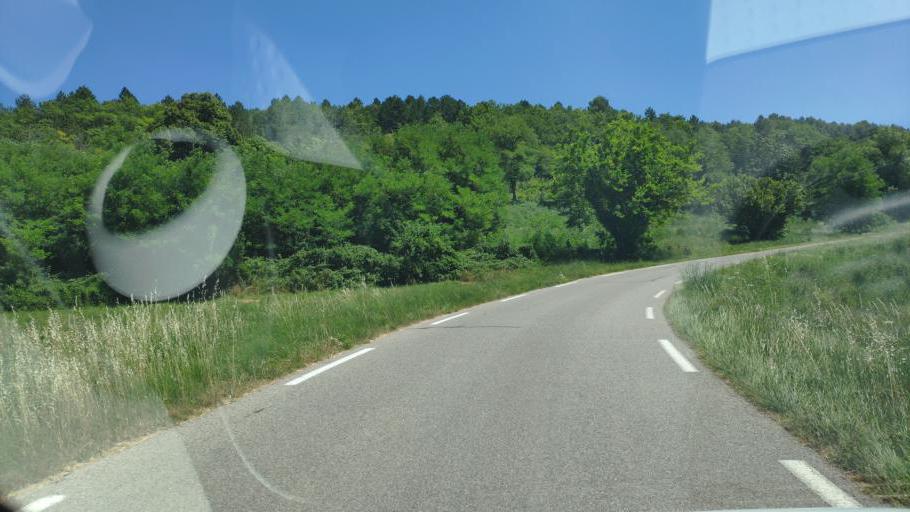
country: FR
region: Provence-Alpes-Cote d'Azur
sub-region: Departement du Vaucluse
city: Malaucene
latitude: 44.1771
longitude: 5.1215
